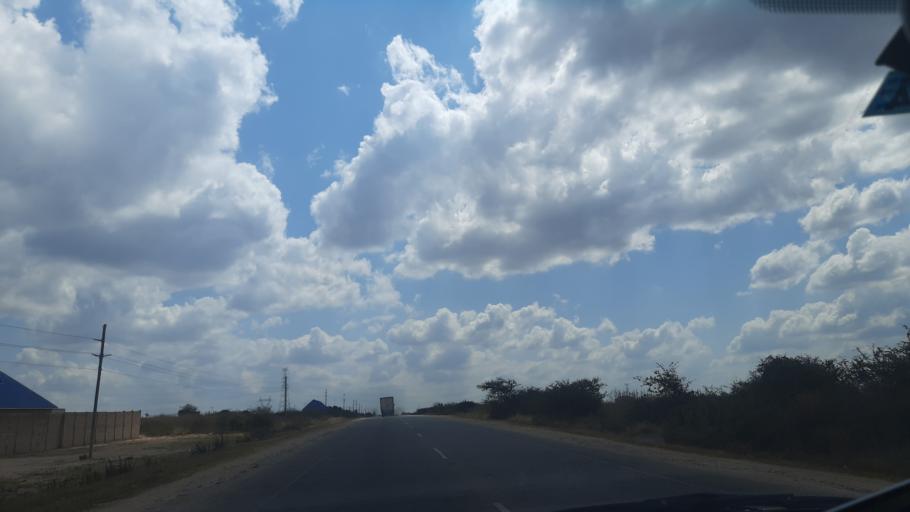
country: TZ
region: Dodoma
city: Dodoma
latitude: -6.1259
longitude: 35.6733
